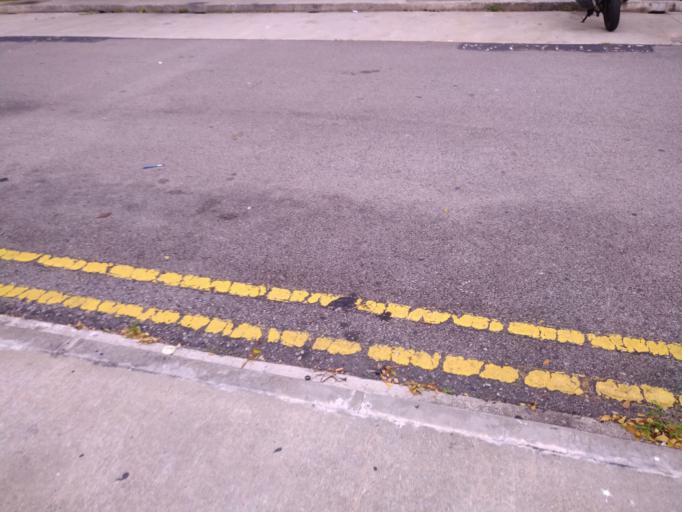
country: SG
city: Singapore
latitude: 1.2864
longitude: 103.8200
